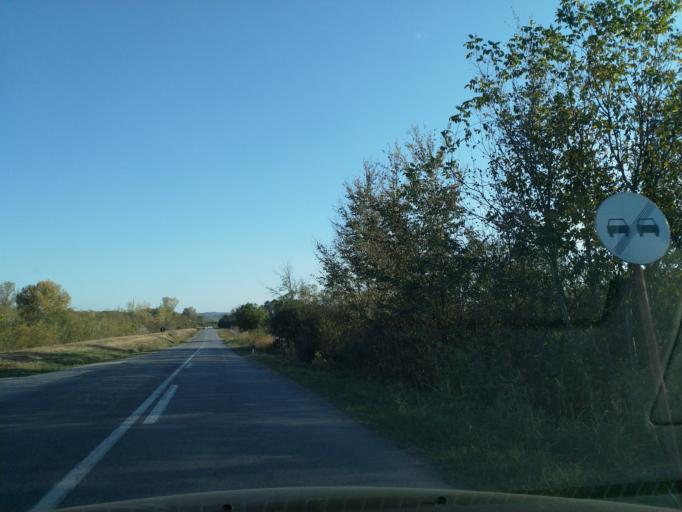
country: RS
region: Central Serbia
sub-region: Pomoravski Okrug
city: Svilajnac
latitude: 44.2286
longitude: 21.1453
